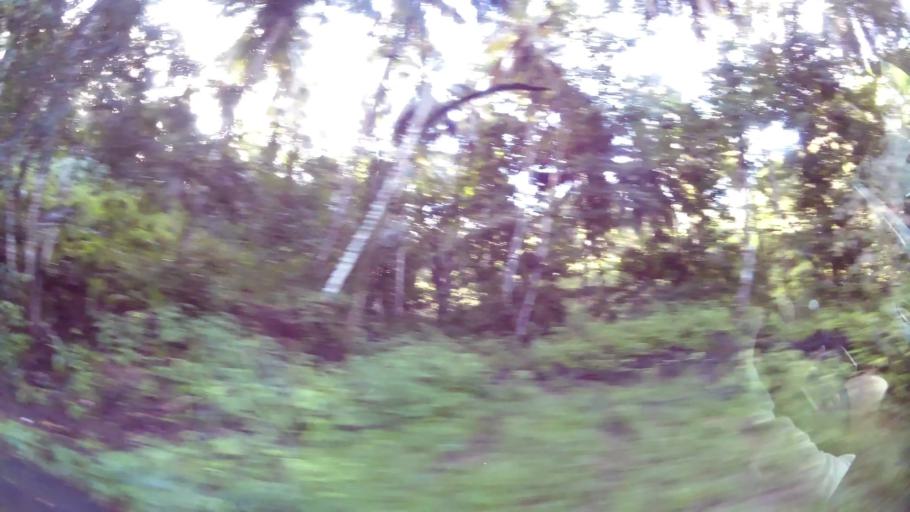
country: DM
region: Saint Andrew
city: Calibishie
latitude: 15.5917
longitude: -61.3750
